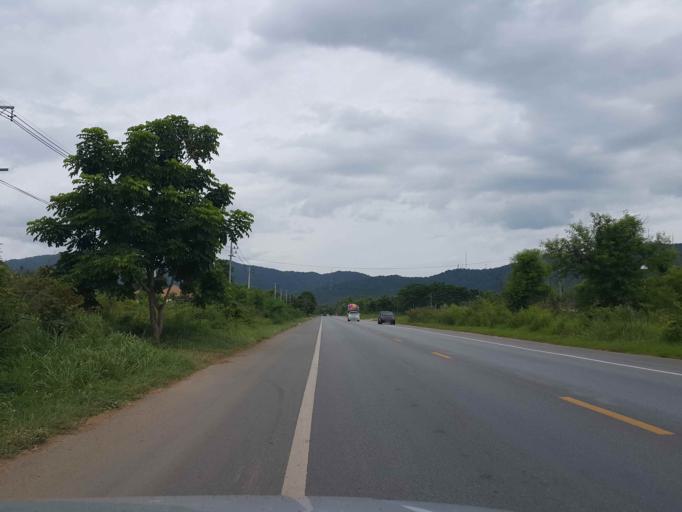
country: TH
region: Lampang
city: Lampang
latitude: 18.2512
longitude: 99.5238
